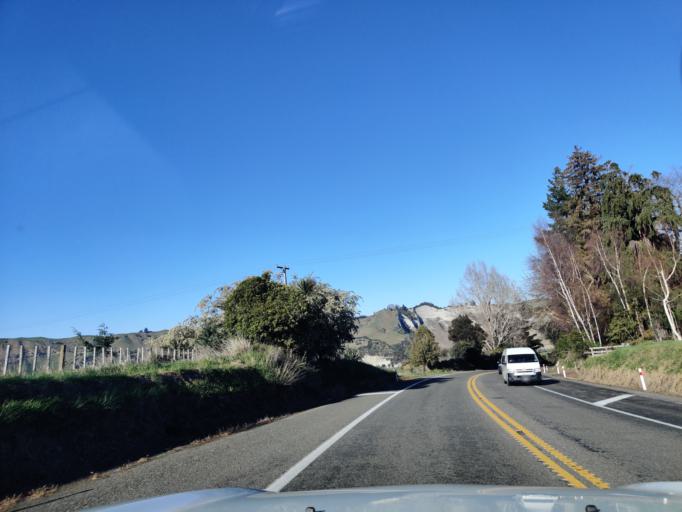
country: NZ
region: Manawatu-Wanganui
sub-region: Ruapehu District
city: Waiouru
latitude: -39.8304
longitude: 175.7819
